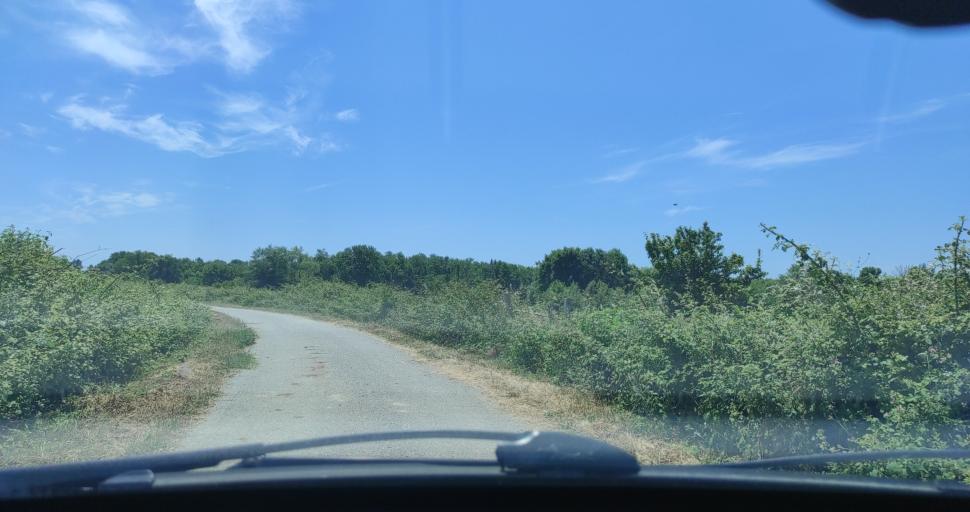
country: AL
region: Shkoder
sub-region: Rrethi i Shkodres
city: Velipoje
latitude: 41.8815
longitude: 19.3832
